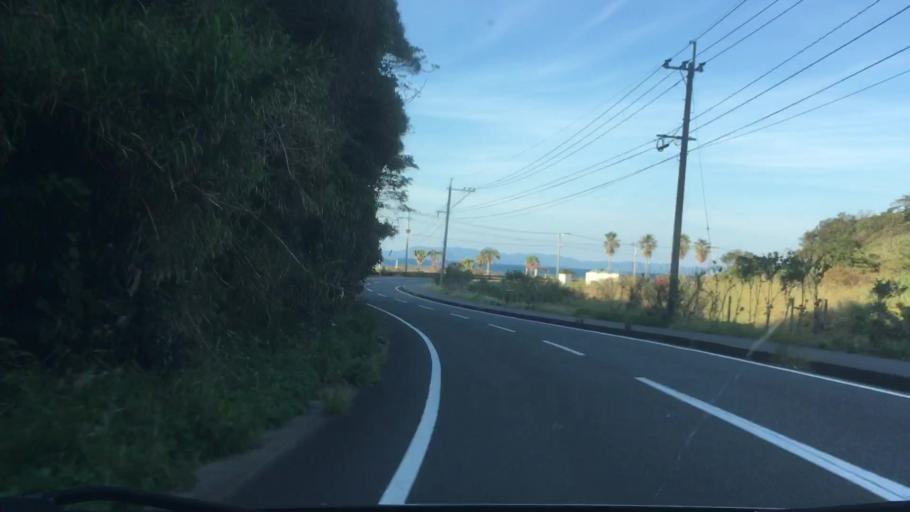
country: JP
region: Nagasaki
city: Sasebo
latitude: 33.0258
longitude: 129.5776
